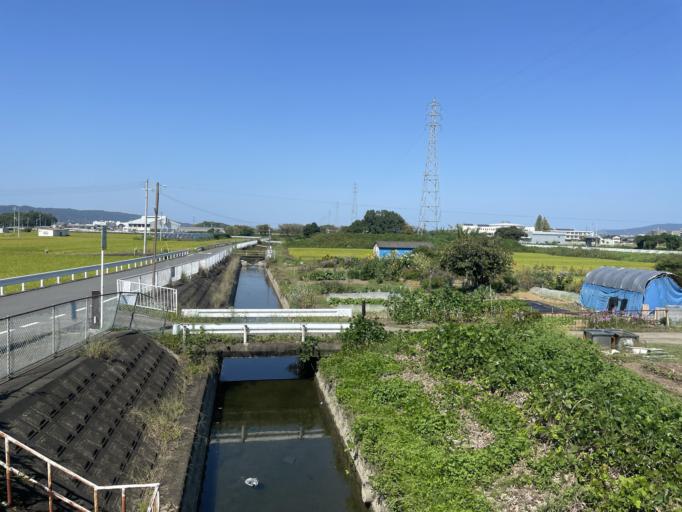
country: JP
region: Nara
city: Tawaramoto
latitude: 34.5694
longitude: 135.7691
